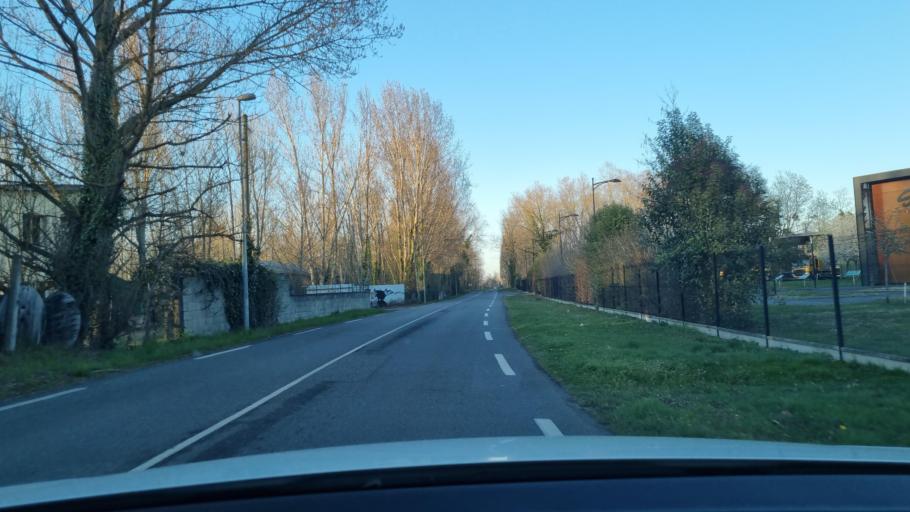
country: FR
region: Midi-Pyrenees
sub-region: Departement des Hautes-Pyrenees
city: Bazet
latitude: 43.2716
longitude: 0.0796
